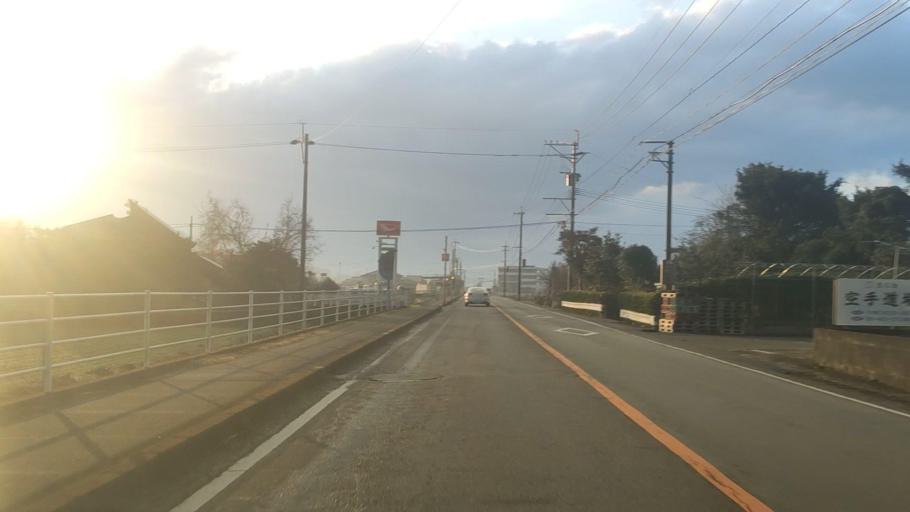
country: JP
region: Kumamoto
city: Uto
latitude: 32.7159
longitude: 130.7727
